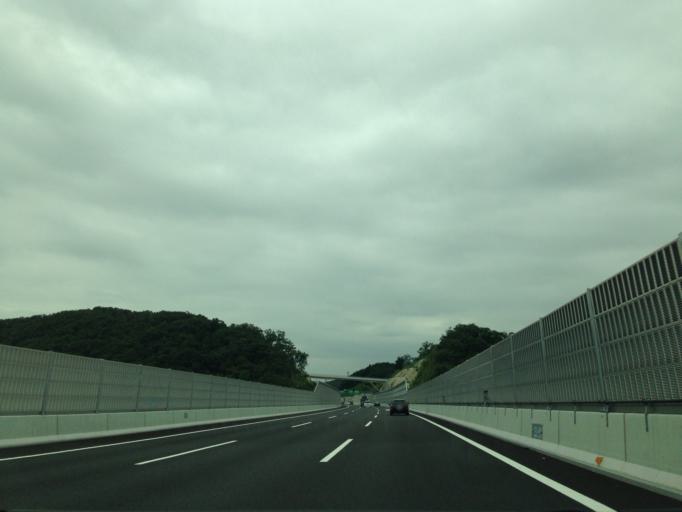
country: JP
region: Aichi
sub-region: Toyota-shi
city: Toyota
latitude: 35.0387
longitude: 137.2132
